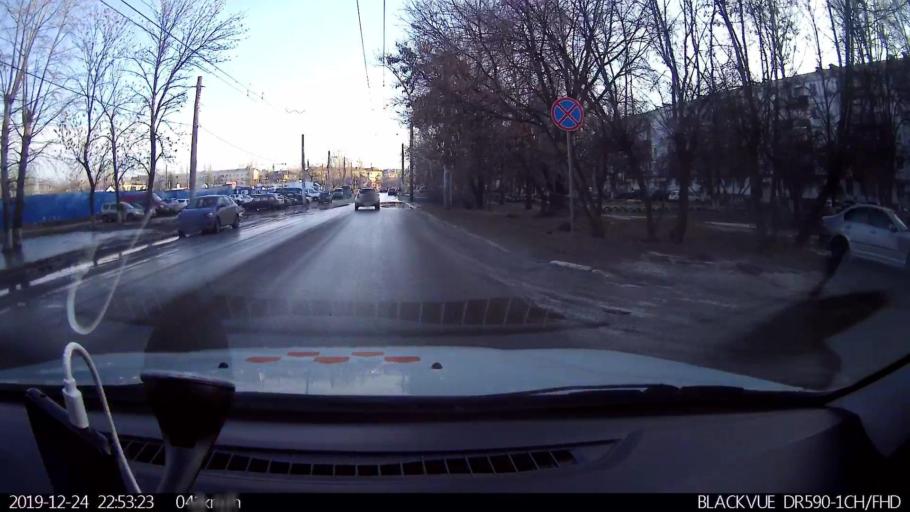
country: RU
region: Nizjnij Novgorod
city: Nizhniy Novgorod
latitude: 56.2850
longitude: 43.9238
